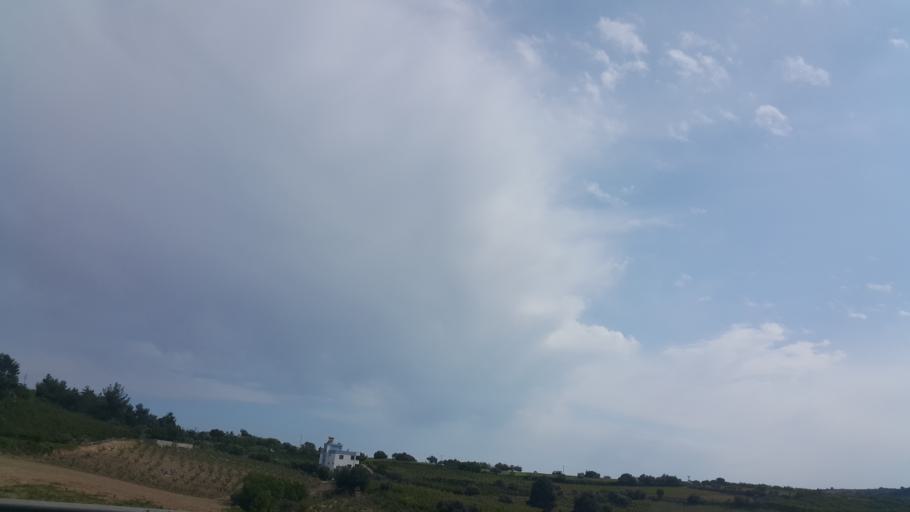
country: TR
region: Mersin
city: Tarsus
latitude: 36.9525
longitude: 34.8293
